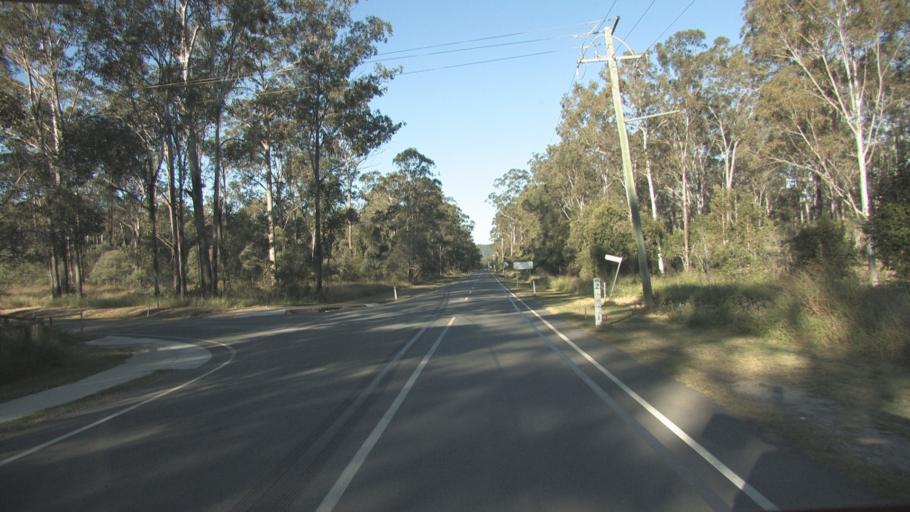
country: AU
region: Queensland
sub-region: Logan
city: Chambers Flat
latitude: -27.7678
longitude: 153.1217
